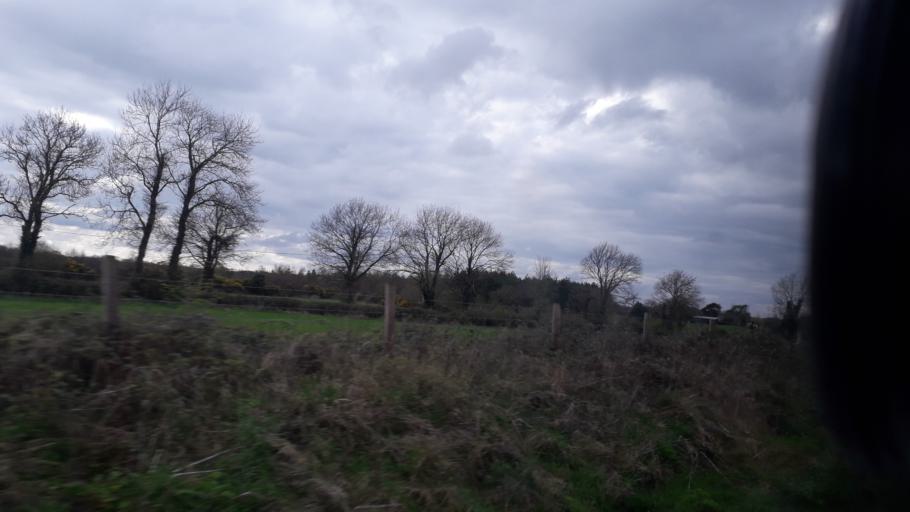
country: IE
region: Leinster
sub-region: An Iarmhi
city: Castlepollard
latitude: 53.6493
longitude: -7.4279
